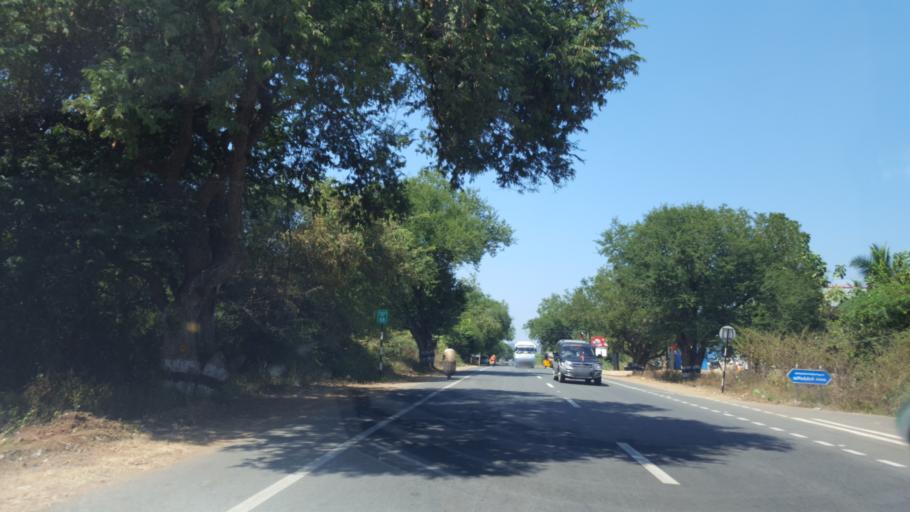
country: IN
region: Tamil Nadu
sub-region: Kancheepuram
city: Karumbakkam
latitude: 12.6257
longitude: 80.0520
